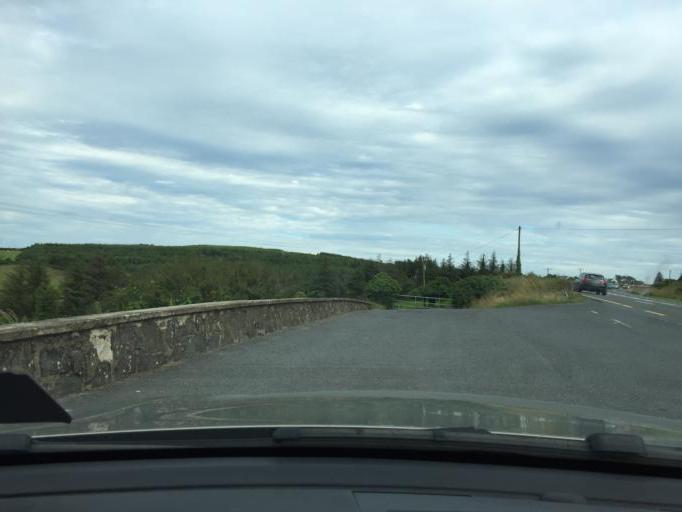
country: IE
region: Munster
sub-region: Waterford
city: Dungarvan
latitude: 52.0509
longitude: -7.6617
